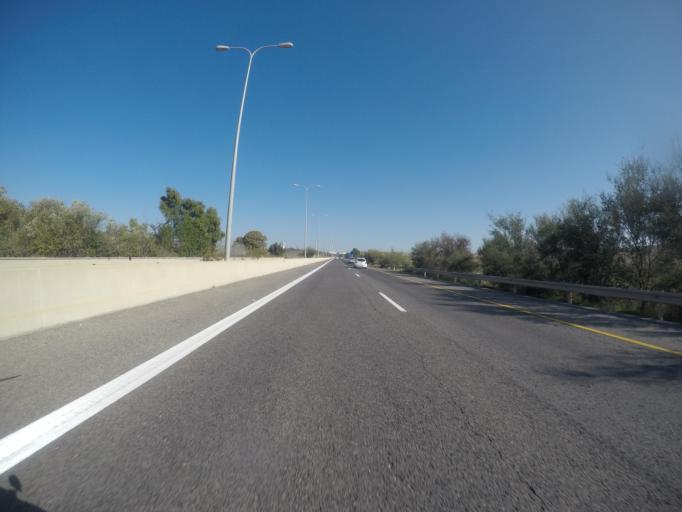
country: IL
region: Haifa
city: El Fureidis
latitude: 32.6062
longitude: 35.0309
